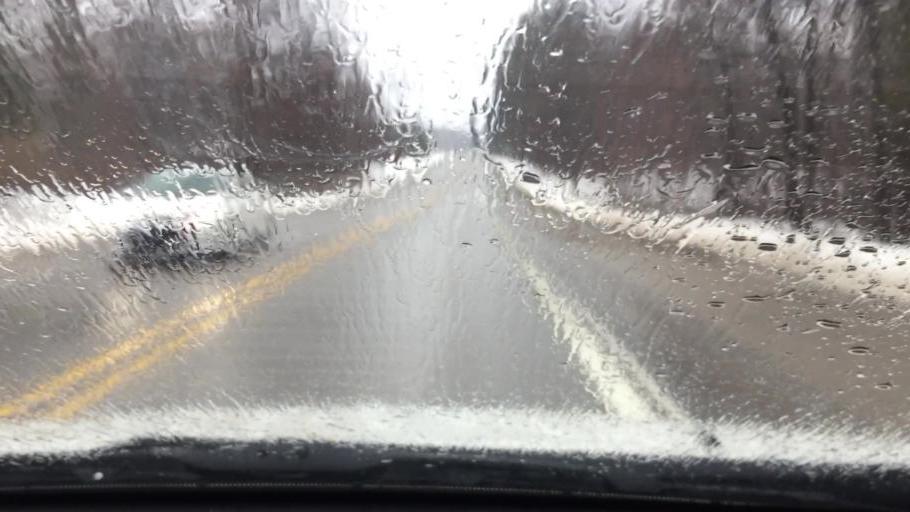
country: US
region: Michigan
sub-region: Charlevoix County
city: East Jordan
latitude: 45.1788
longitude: -85.1640
